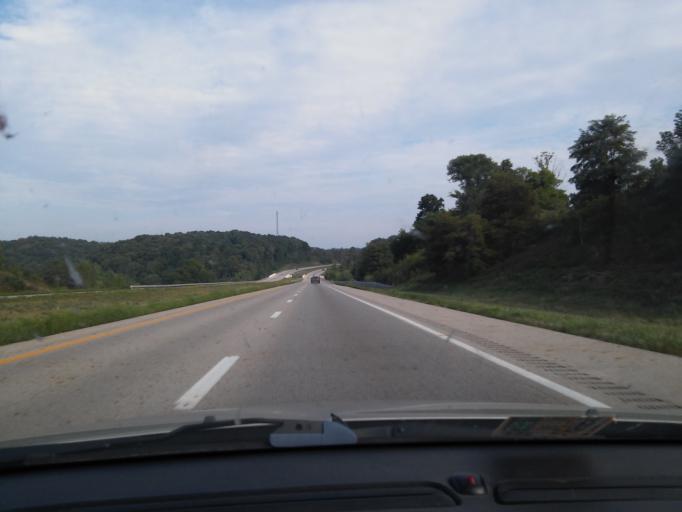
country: US
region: Ohio
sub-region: Ross County
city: Chillicothe
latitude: 39.2581
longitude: -82.8592
